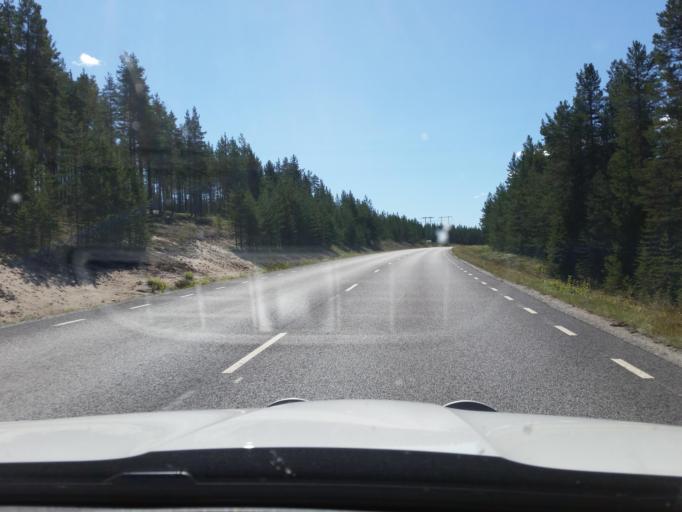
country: SE
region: Norrbotten
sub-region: Pitea Kommun
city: Pitea
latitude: 65.2651
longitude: 21.5361
